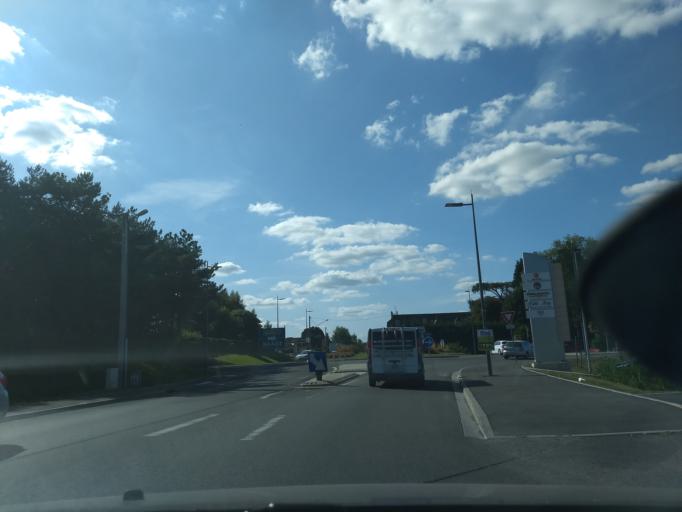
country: FR
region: Aquitaine
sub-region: Departement des Pyrenees-Atlantiques
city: Idron
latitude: 43.3031
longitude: -0.3210
